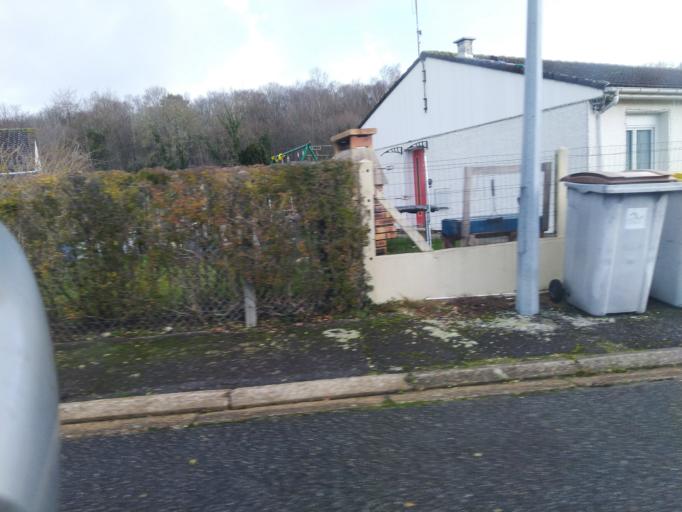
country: FR
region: Haute-Normandie
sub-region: Departement de la Seine-Maritime
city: Yainville
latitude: 49.4481
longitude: 0.8316
